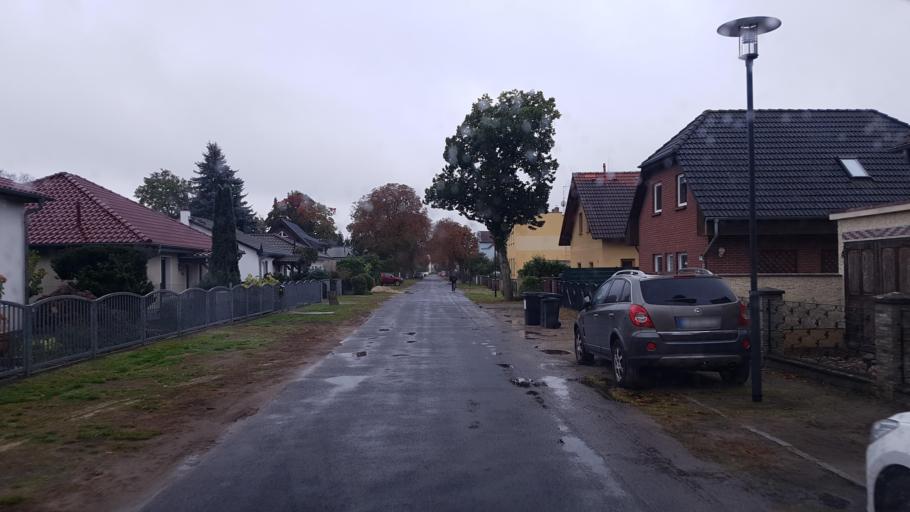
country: DE
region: Brandenburg
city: Furstenwalde
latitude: 52.3475
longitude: 14.0674
